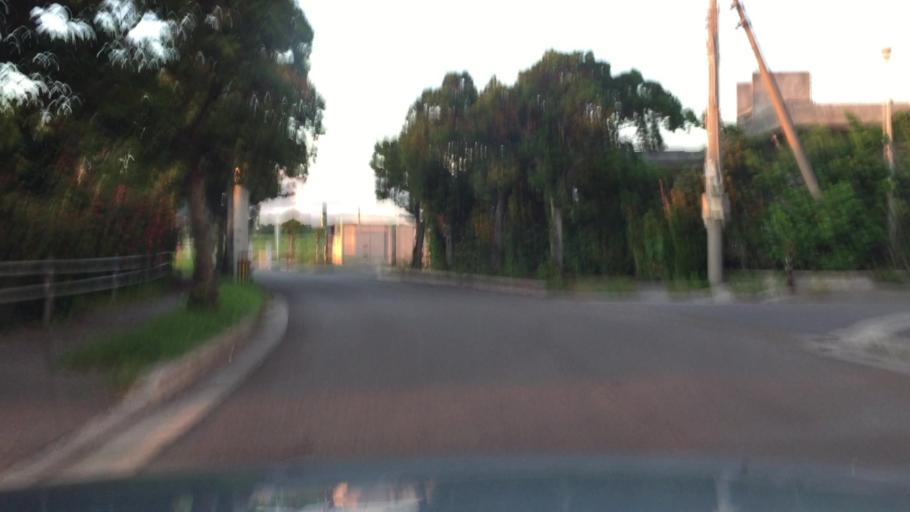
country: JP
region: Okinawa
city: Ishigaki
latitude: 24.3505
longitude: 124.1647
